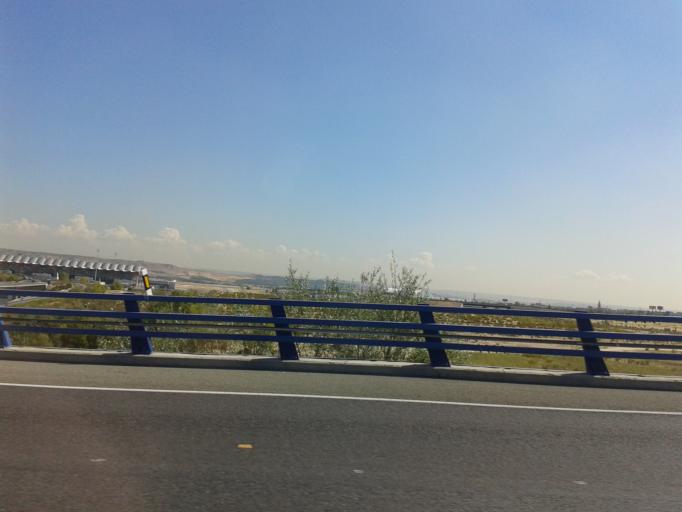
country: ES
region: Madrid
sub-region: Provincia de Madrid
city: Barajas de Madrid
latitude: 40.4852
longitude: -3.6010
